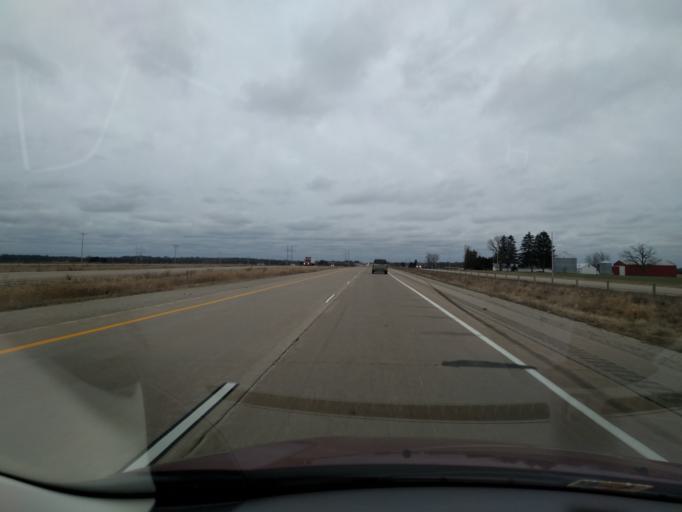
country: US
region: Wisconsin
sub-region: Winnebago County
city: Winneconne
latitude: 44.1790
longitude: -88.6646
